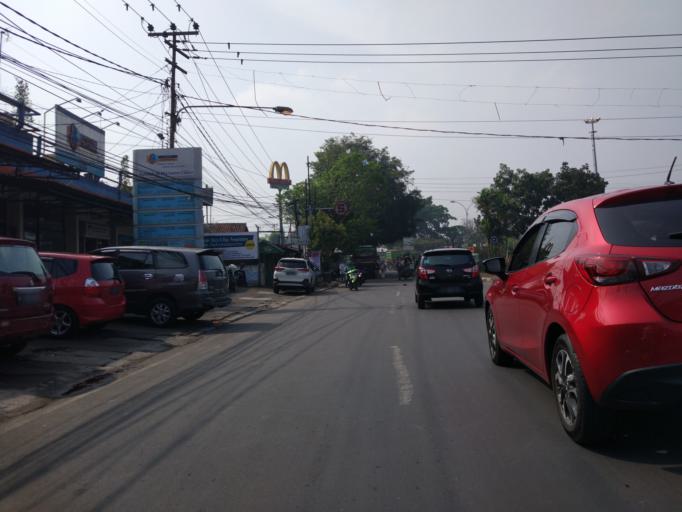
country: ID
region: West Java
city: Cileunyi
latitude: -6.9343
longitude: 107.7171
